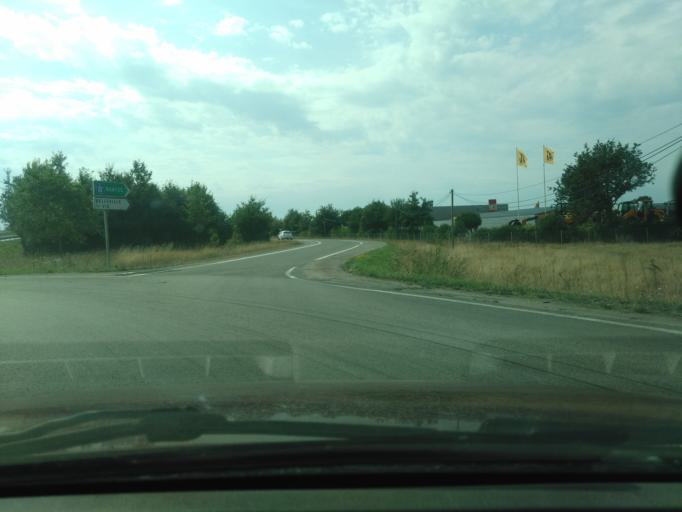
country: FR
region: Pays de la Loire
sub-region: Departement de la Vendee
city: Mouilleron-le-Captif
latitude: 46.7450
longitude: -1.4267
